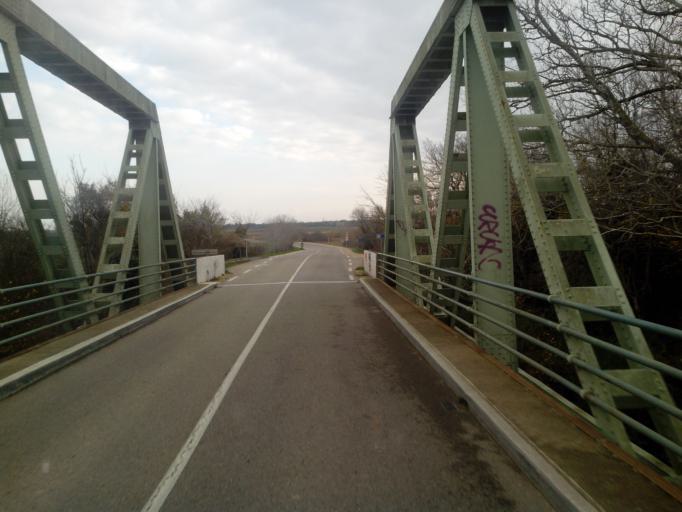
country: FR
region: Provence-Alpes-Cote d'Azur
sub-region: Departement des Bouches-du-Rhone
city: Saintes-Maries-de-la-Mer
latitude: 43.5464
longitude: 4.3501
